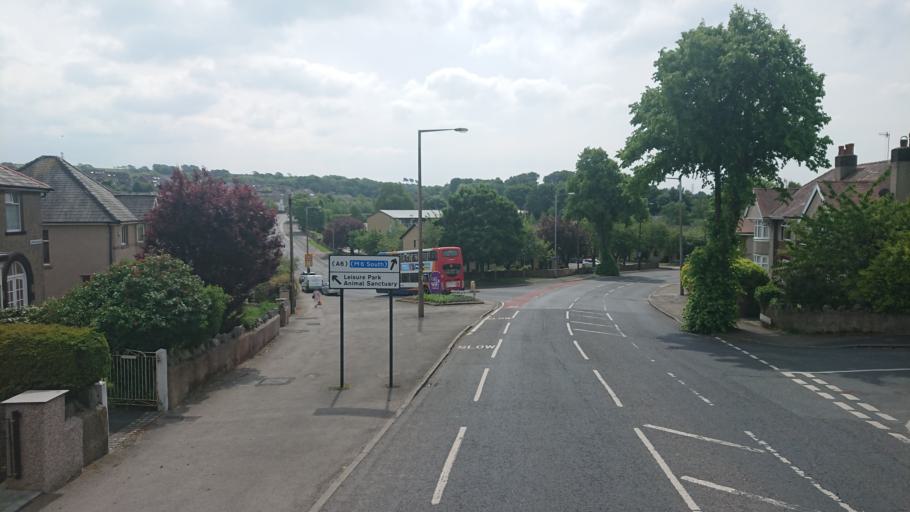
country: GB
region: England
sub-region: Lancashire
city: Lancaster
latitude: 54.0350
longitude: -2.7873
